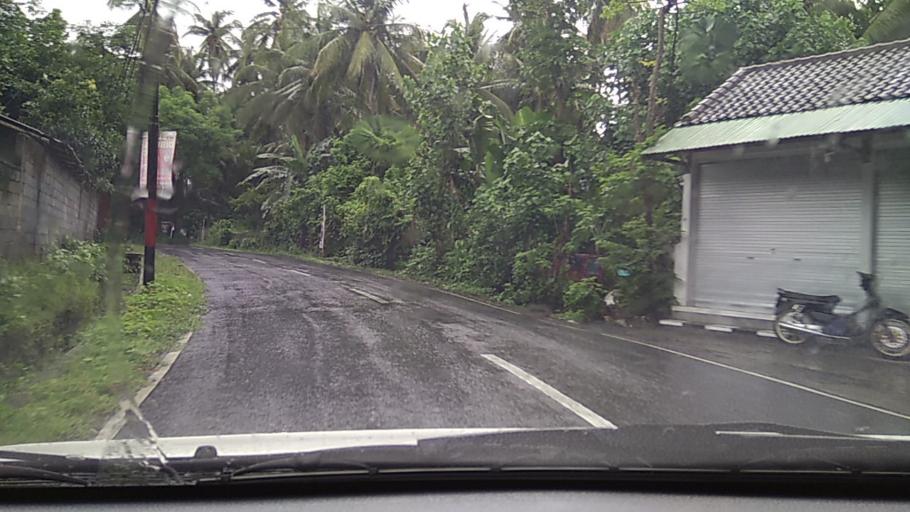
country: ID
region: Bali
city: Banjar Timbrah
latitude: -8.4740
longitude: 115.6193
